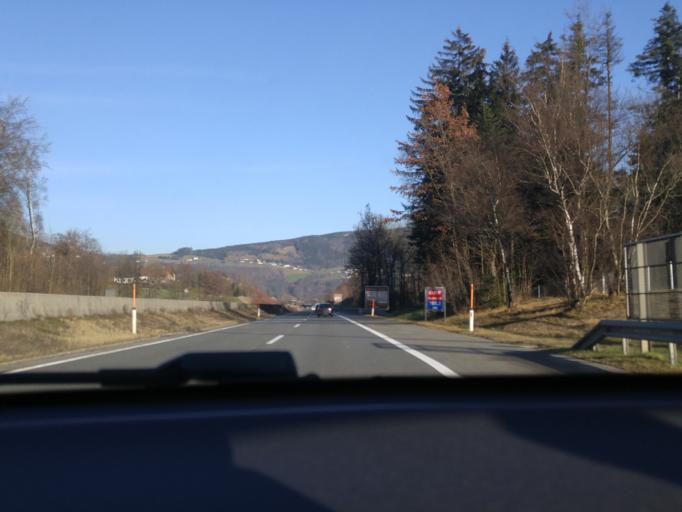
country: AT
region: Upper Austria
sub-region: Politischer Bezirk Vocklabruck
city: Mondsee
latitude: 47.8478
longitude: 13.3195
